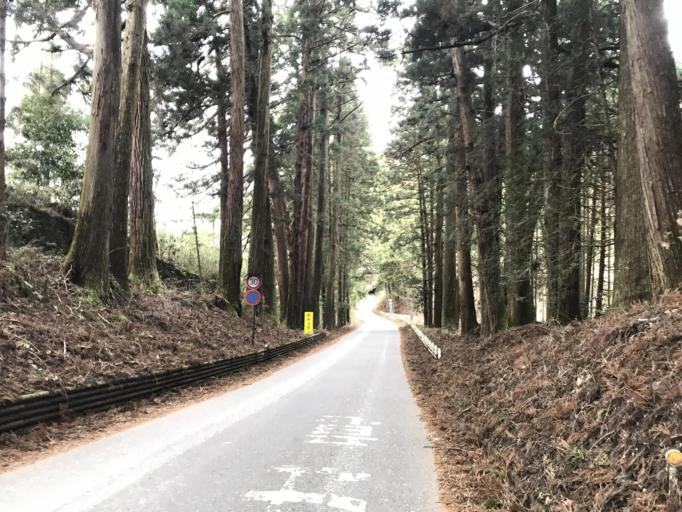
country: JP
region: Tochigi
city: Imaichi
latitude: 36.6993
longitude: 139.7084
